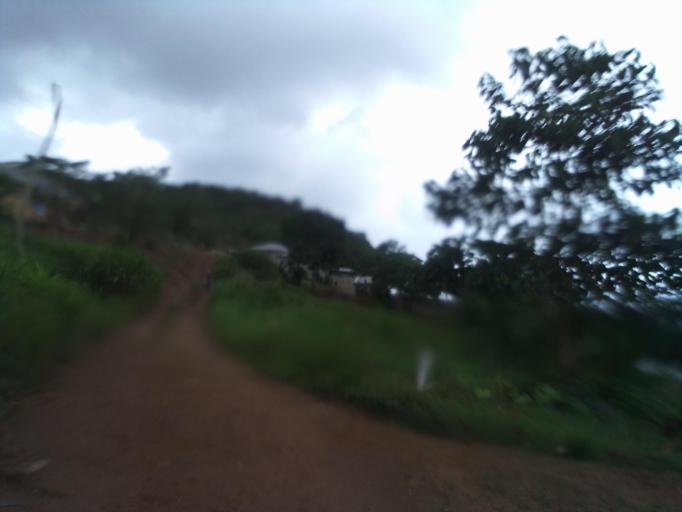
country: SL
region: Eastern Province
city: Kenema
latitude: 7.8507
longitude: -11.1863
